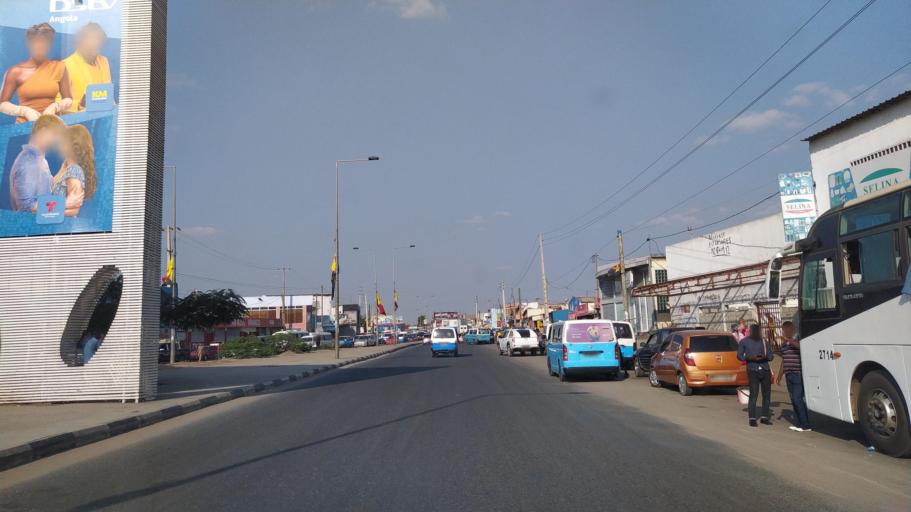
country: AO
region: Luanda
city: Luanda
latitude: -8.8777
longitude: 13.2782
